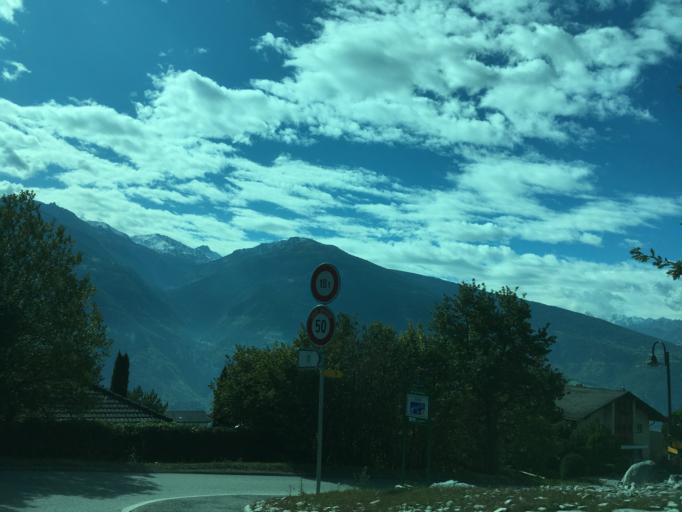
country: CH
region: Valais
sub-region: Sierre District
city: Chermignon-d'en Haut
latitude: 46.2858
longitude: 7.4869
